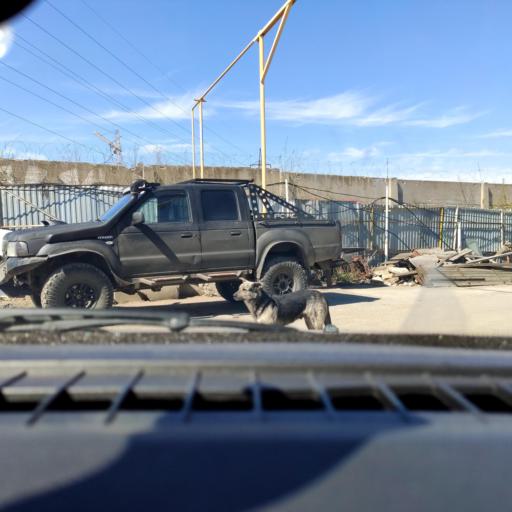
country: RU
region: Samara
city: Samara
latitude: 53.1992
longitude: 50.2362
